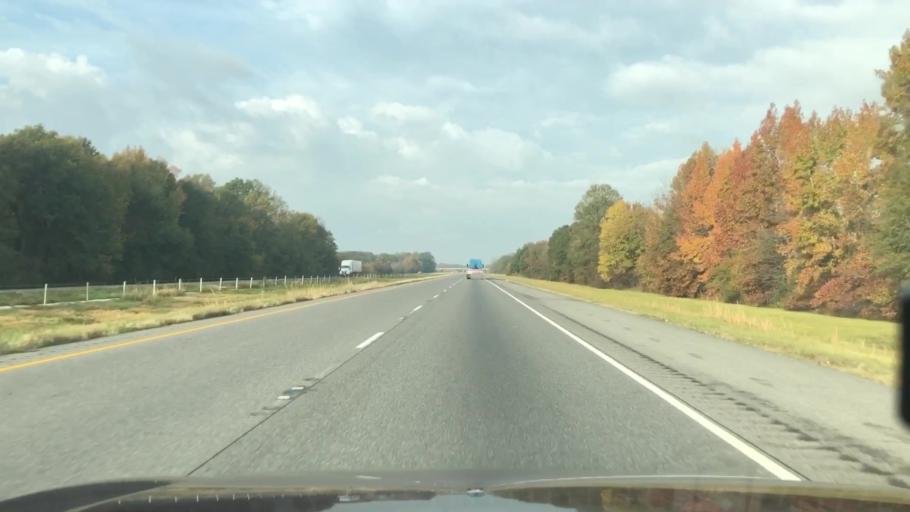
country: US
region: Louisiana
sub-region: Richland Parish
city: Delhi
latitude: 32.4238
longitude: -91.3562
